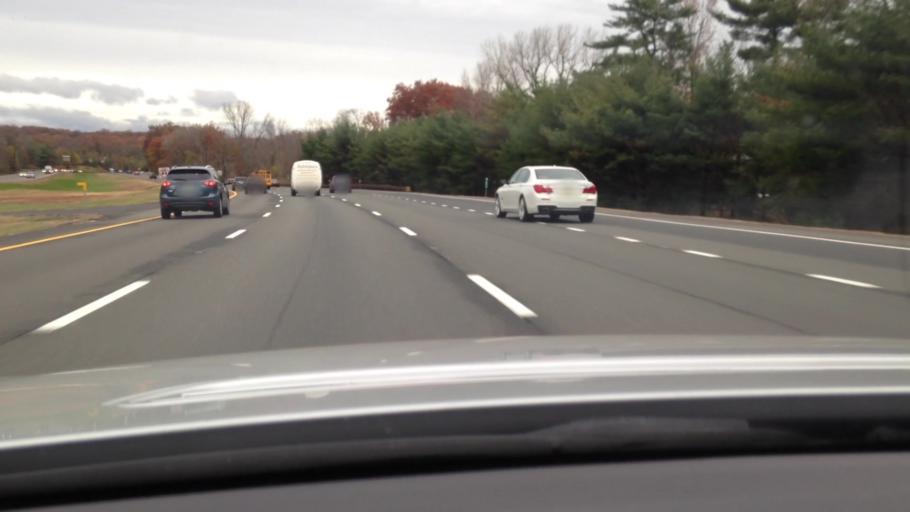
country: US
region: New Jersey
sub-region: Bergen County
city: Paramus
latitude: 40.9699
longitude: -74.0651
